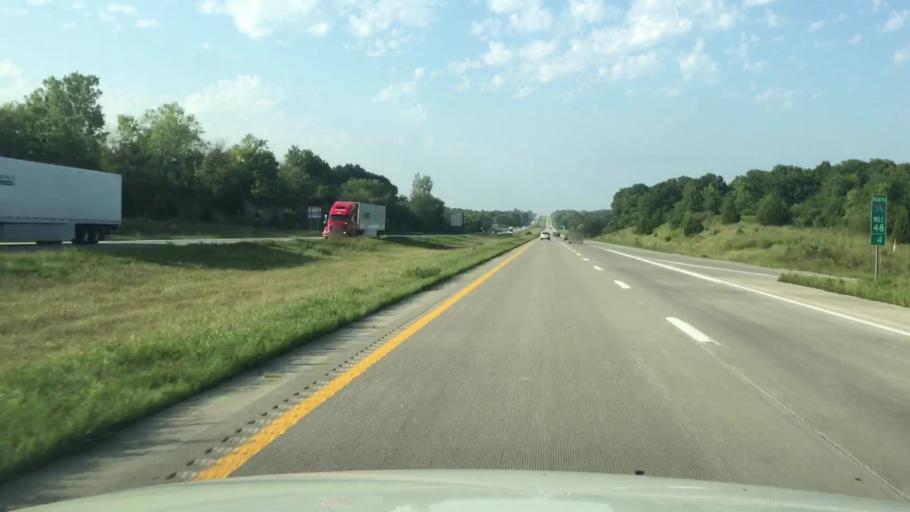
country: US
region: Missouri
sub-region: Clinton County
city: Cameron
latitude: 39.6702
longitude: -94.2349
